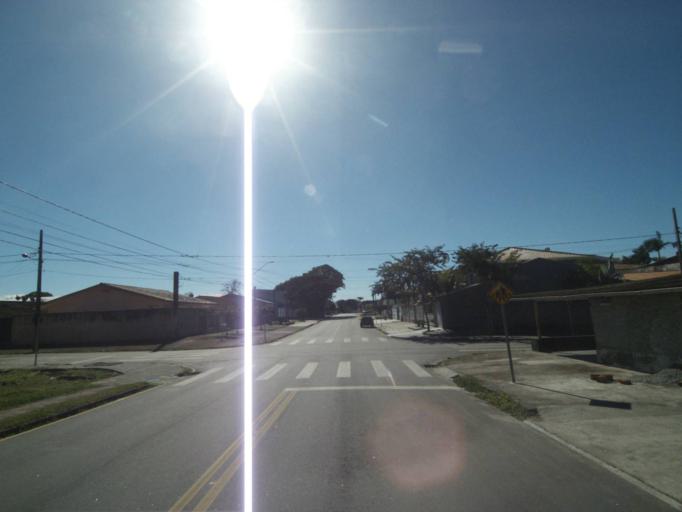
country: BR
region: Parana
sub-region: Paranagua
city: Paranagua
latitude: -25.5327
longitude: -48.5285
